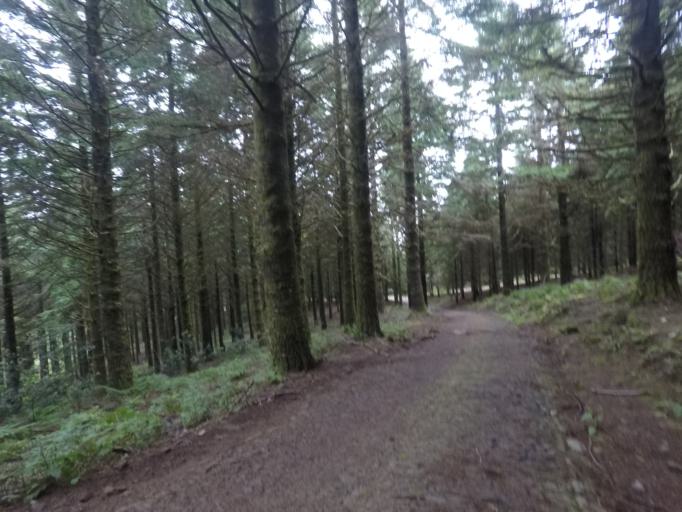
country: PT
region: Madeira
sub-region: Funchal
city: Nossa Senhora do Monte
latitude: 32.7195
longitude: -16.8857
